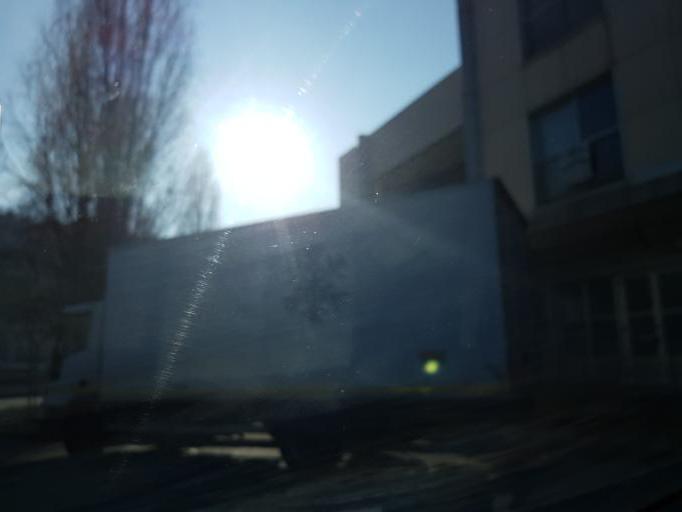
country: IT
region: Liguria
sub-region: Provincia di Genova
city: Manesseno
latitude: 44.4700
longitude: 8.9049
